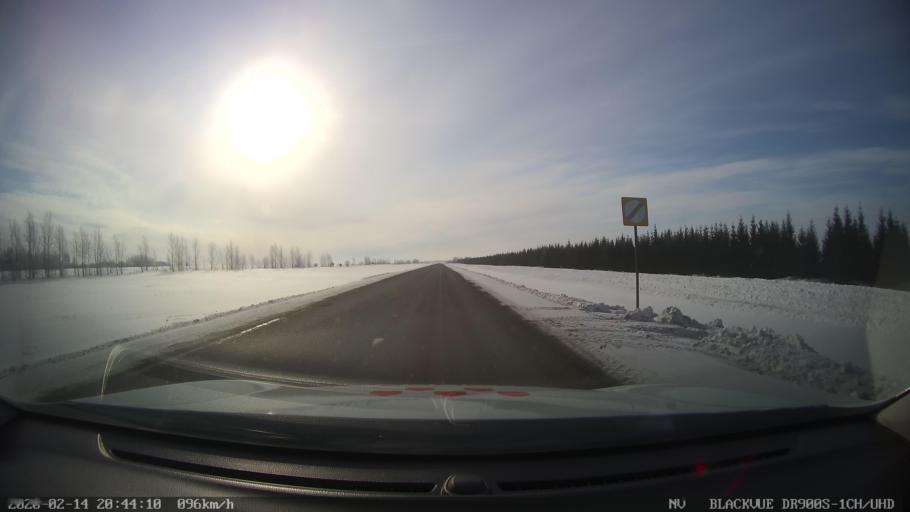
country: RU
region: Tatarstan
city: Kuybyshevskiy Zaton
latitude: 55.2979
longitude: 49.1469
